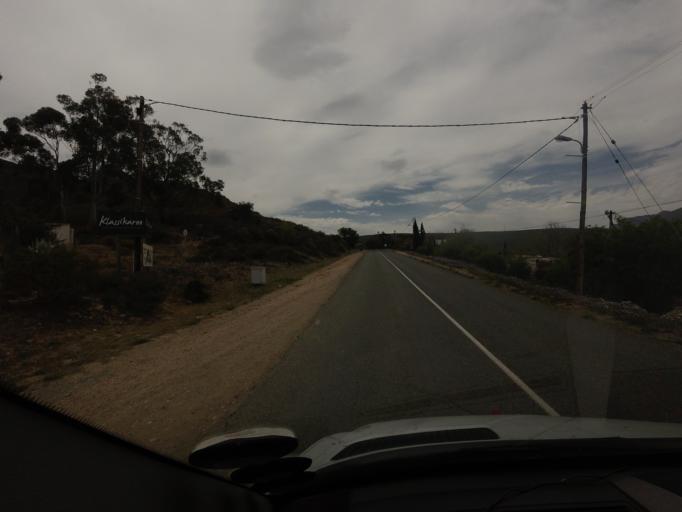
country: ZA
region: Western Cape
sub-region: Overberg District Municipality
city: Swellendam
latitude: -33.9013
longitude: 20.7214
